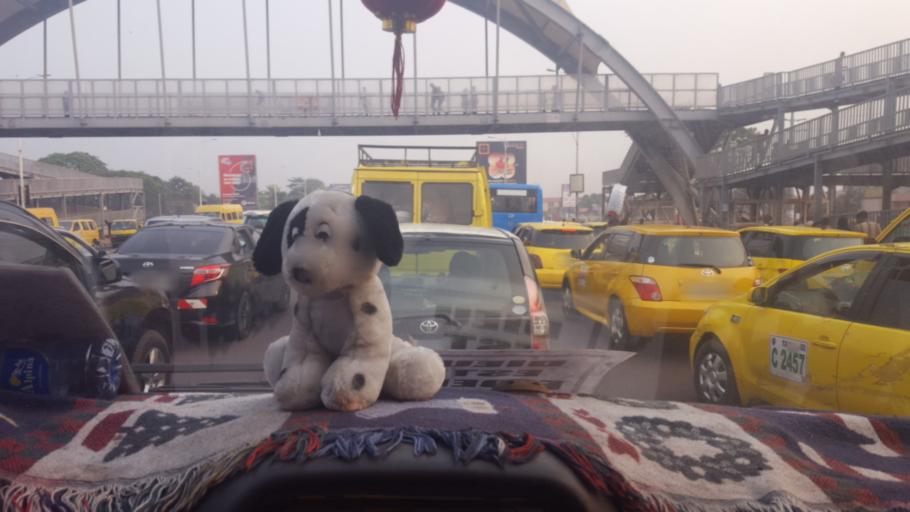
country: CD
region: Kinshasa
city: Kinshasa
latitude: -4.3523
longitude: 15.3350
